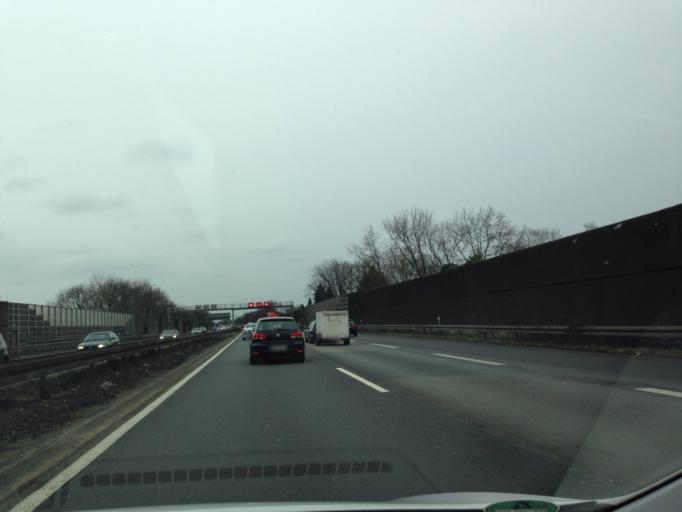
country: DE
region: North Rhine-Westphalia
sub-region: Regierungsbezirk Dusseldorf
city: Krefeld
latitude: 51.3480
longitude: 6.6254
